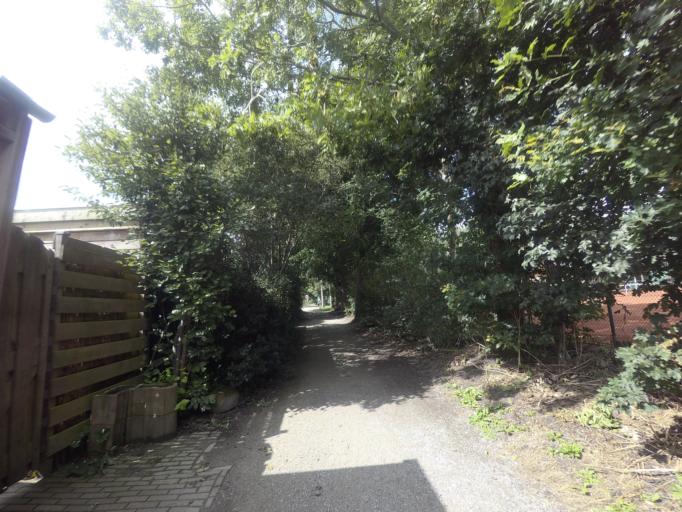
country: NL
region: Friesland
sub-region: Gemeente Skarsterlan
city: Joure
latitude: 52.9523
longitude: 5.8310
